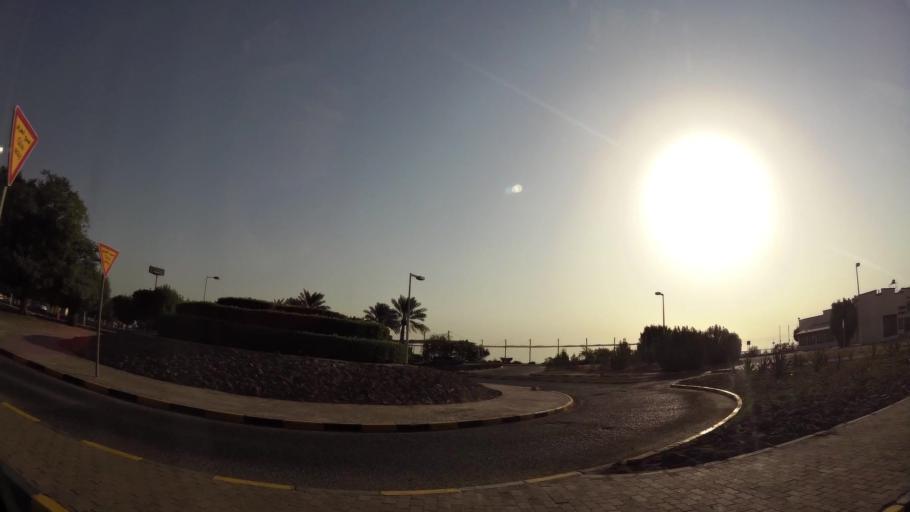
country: KW
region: Al Asimah
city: Ad Dasmah
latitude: 29.3808
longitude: 48.0032
